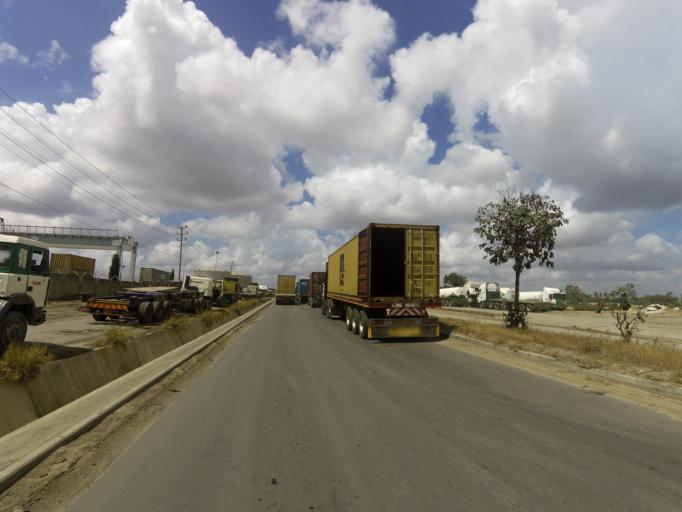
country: TZ
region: Dar es Salaam
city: Dar es Salaam
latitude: -6.8528
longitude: 39.2917
